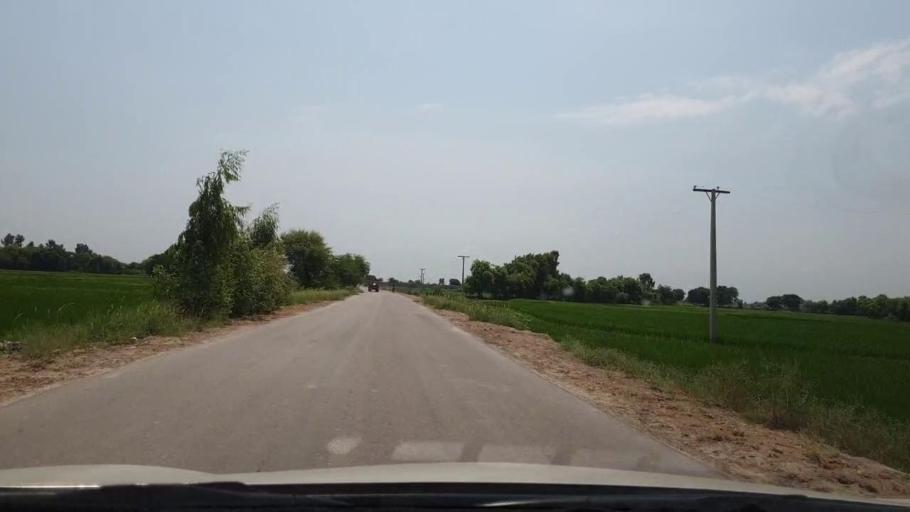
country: PK
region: Sindh
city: Ratodero
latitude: 27.8173
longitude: 68.2471
